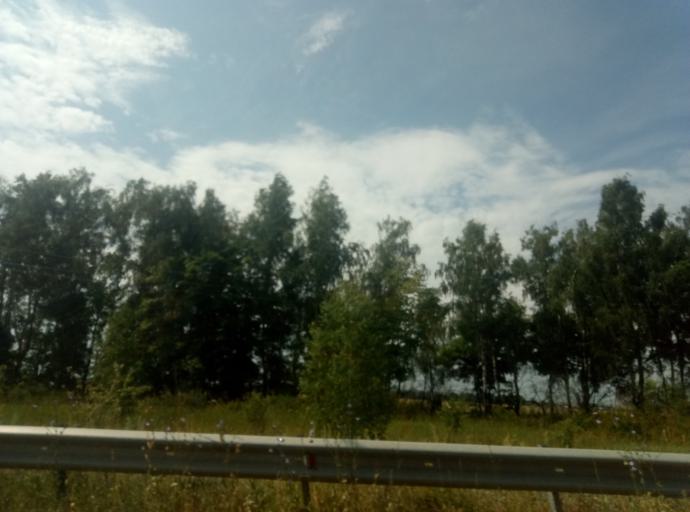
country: RU
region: Tula
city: Dubovka
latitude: 53.8921
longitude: 38.0477
